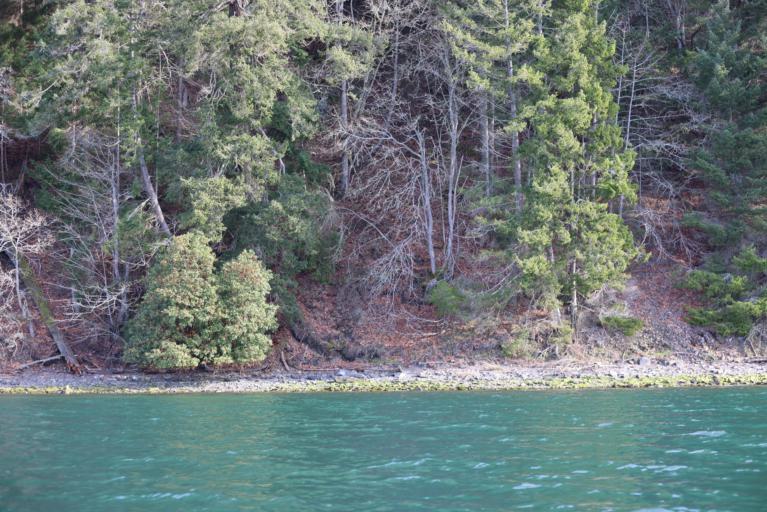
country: CA
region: British Columbia
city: Duncan
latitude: 48.7597
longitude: -123.6130
